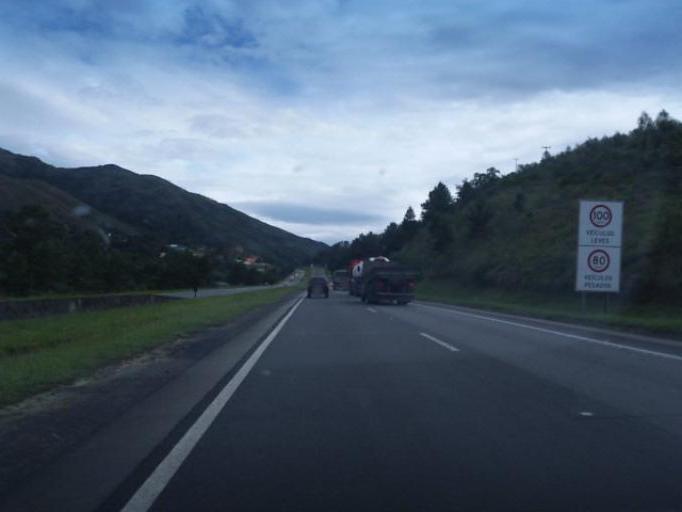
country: BR
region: Parana
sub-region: Campina Grande Do Sul
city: Campina Grande do Sul
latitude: -25.1282
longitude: -48.8575
